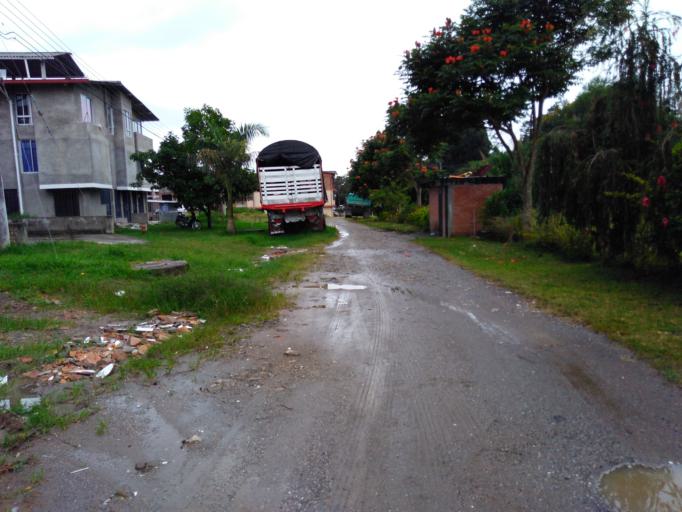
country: CO
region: Cauca
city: Popayan
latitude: 2.4512
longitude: -76.5925
